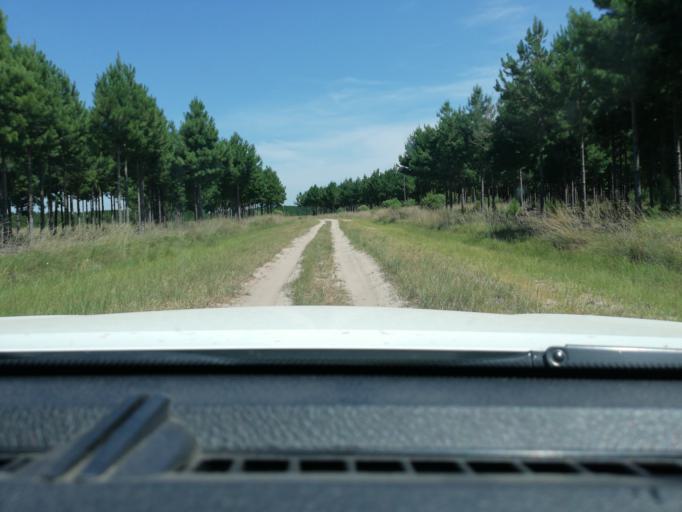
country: AR
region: Corrientes
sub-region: Departamento de San Miguel
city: San Miguel
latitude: -28.0317
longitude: -57.4690
